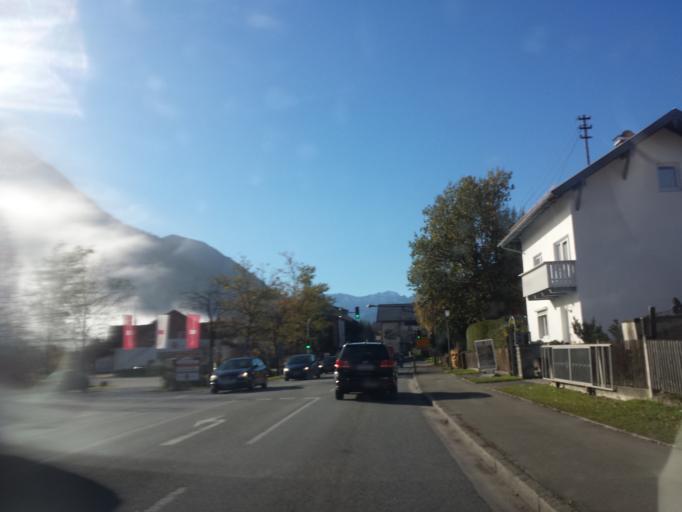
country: DE
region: Bavaria
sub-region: Upper Bavaria
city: Oberau
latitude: 47.5613
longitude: 11.1389
